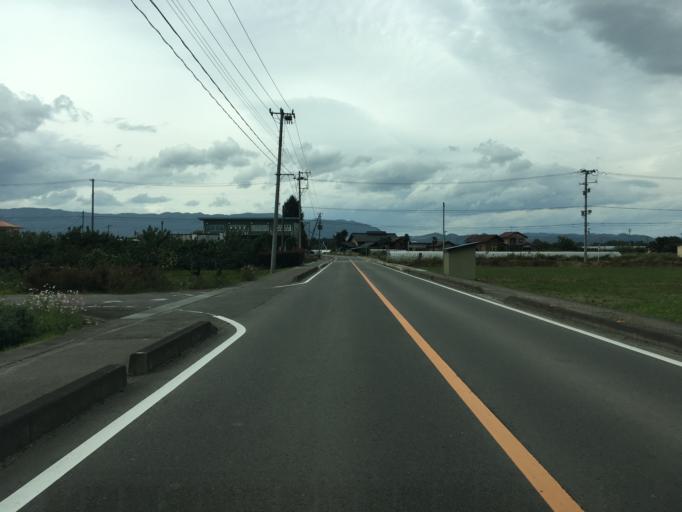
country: JP
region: Fukushima
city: Hobaramachi
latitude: 37.8350
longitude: 140.5586
